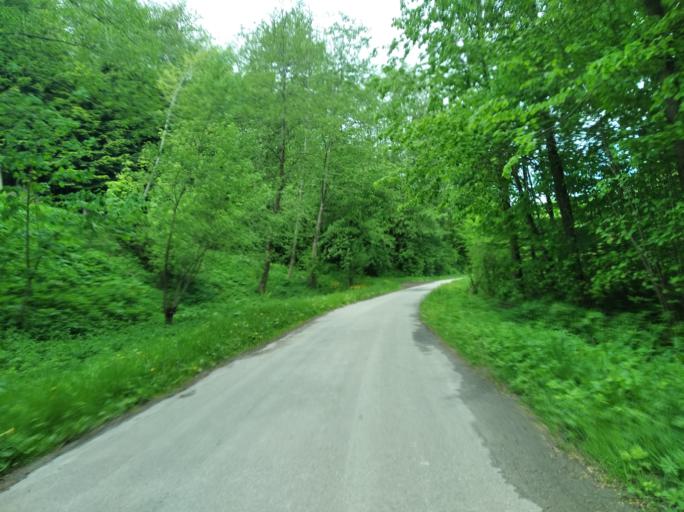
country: PL
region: Subcarpathian Voivodeship
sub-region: Powiat strzyzowski
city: Strzyzow
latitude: 49.9158
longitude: 21.7593
